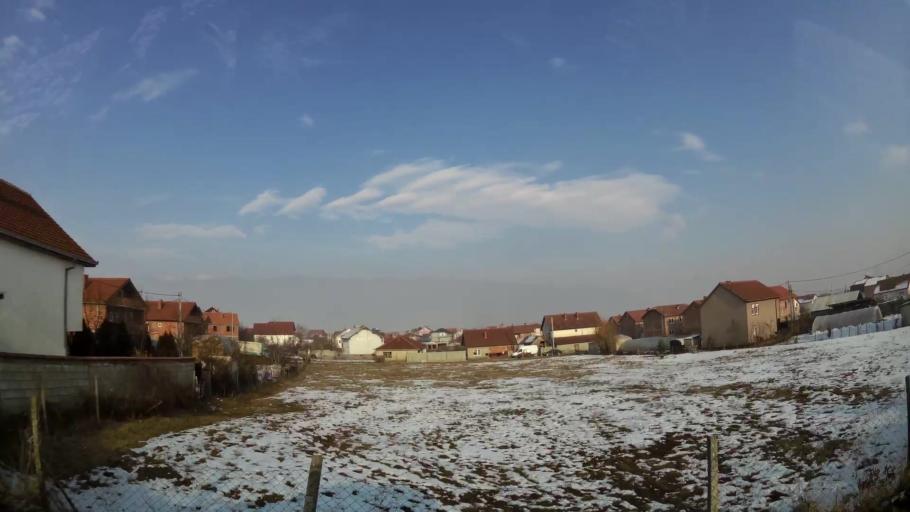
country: MK
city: Creshevo
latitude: 42.0207
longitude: 21.4993
